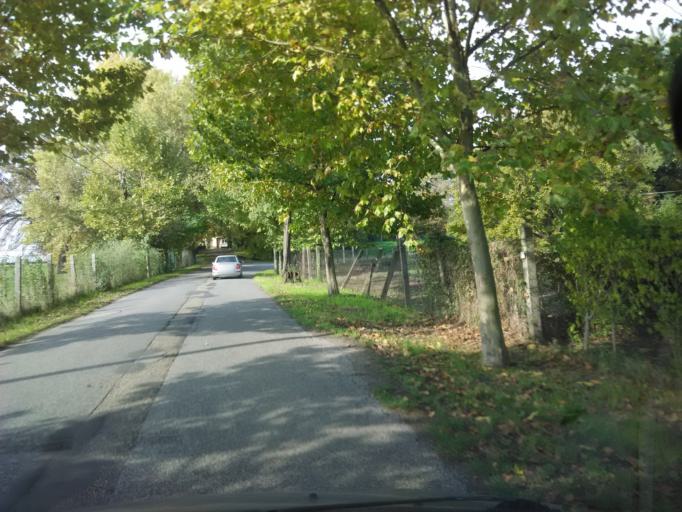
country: HU
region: Komarom-Esztergom
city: Komarom
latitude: 47.7570
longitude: 18.0989
